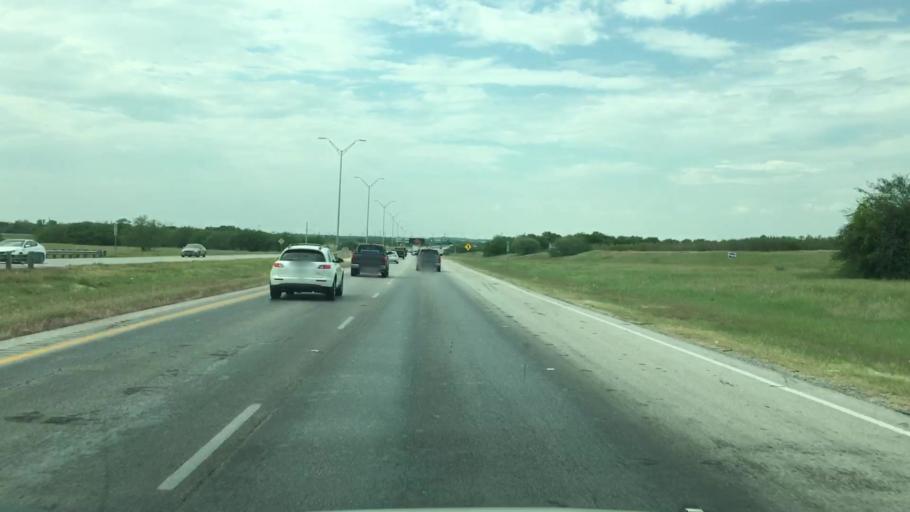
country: US
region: Texas
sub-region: Bexar County
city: Elmendorf
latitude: 29.3078
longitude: -98.3996
